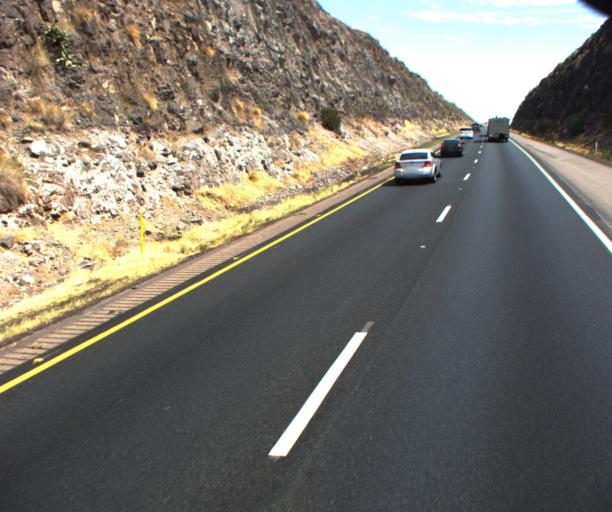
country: US
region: Arizona
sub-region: Yavapai County
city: Black Canyon City
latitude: 34.1573
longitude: -112.1381
